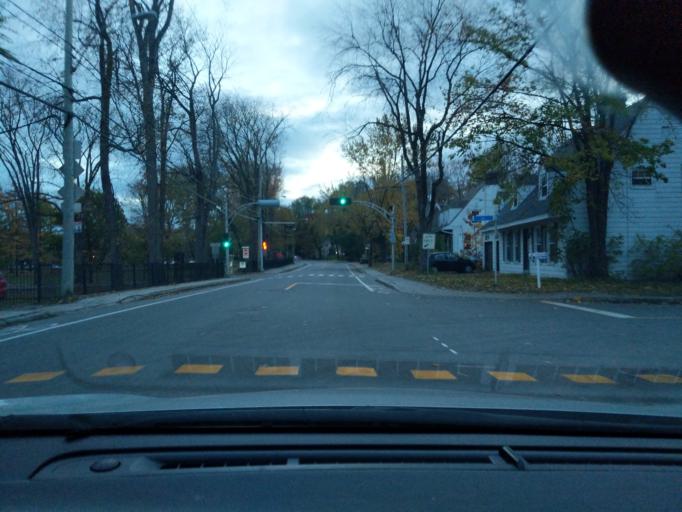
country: CA
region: Quebec
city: Quebec
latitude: 46.7786
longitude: -71.2506
